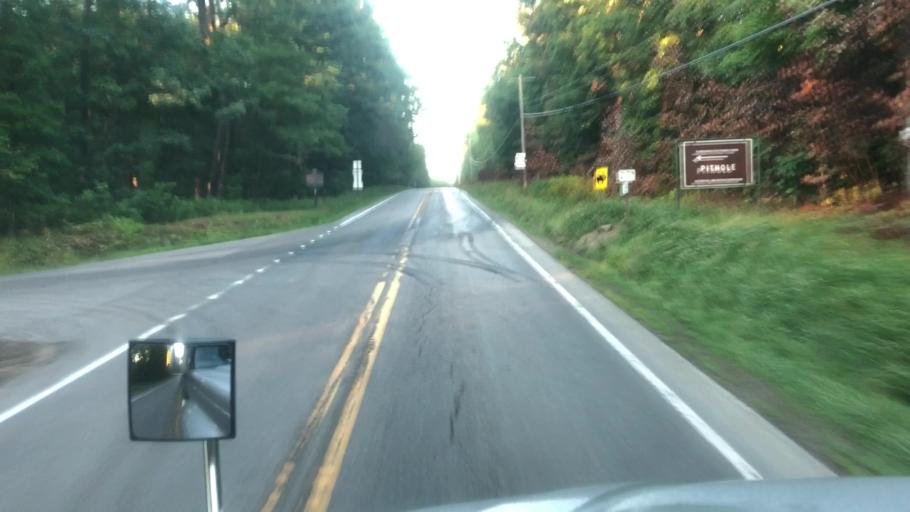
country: US
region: Pennsylvania
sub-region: Venango County
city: Hasson Heights
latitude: 41.5176
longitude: -79.6189
